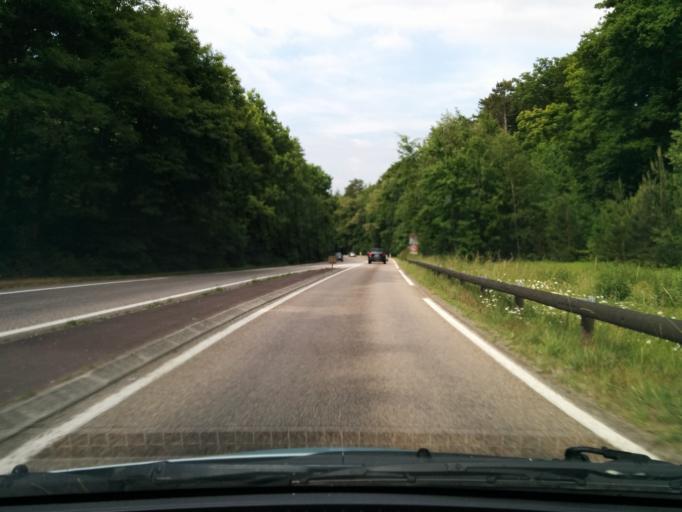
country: FR
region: Haute-Normandie
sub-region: Departement de l'Eure
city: Saint-Aubin-sur-Gaillon
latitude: 49.1407
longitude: 1.3179
